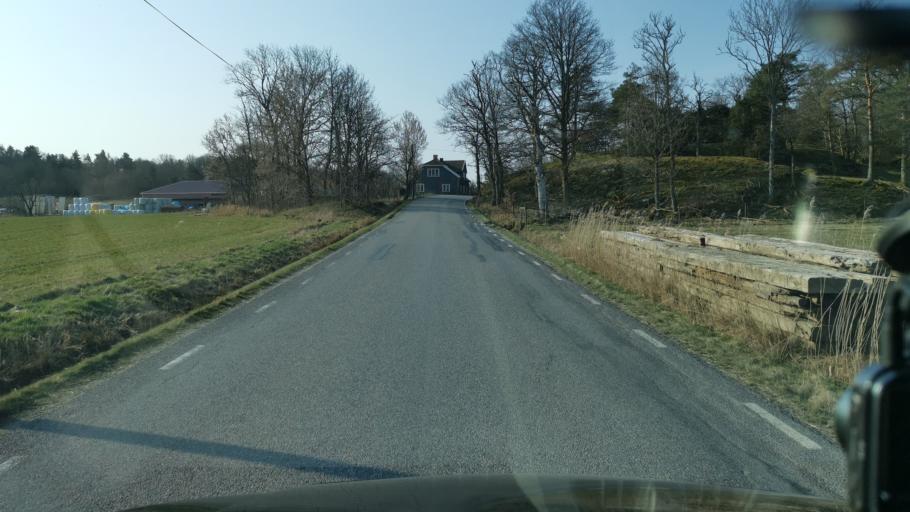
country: SE
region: Vaestra Goetaland
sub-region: Stenungsunds Kommun
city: Stora Hoga
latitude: 57.9734
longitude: 11.8286
